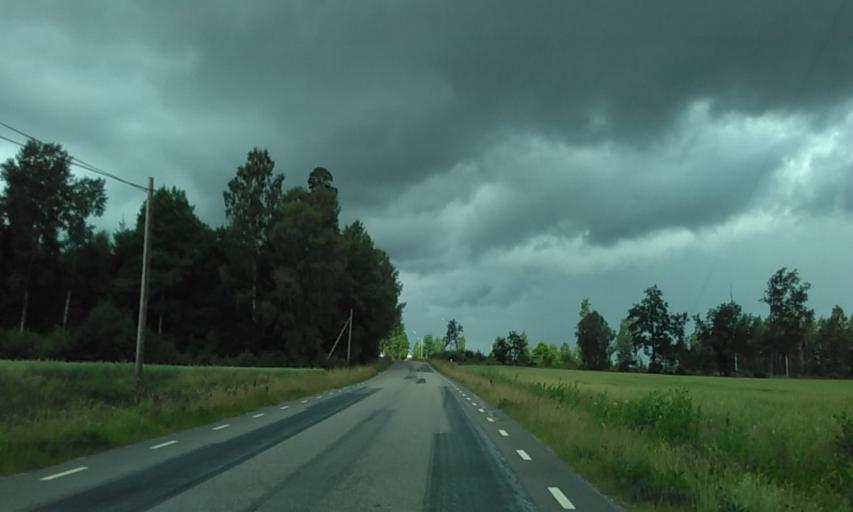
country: SE
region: Vaestra Goetaland
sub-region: Vargarda Kommun
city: Jonstorp
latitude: 58.0049
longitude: 12.7171
